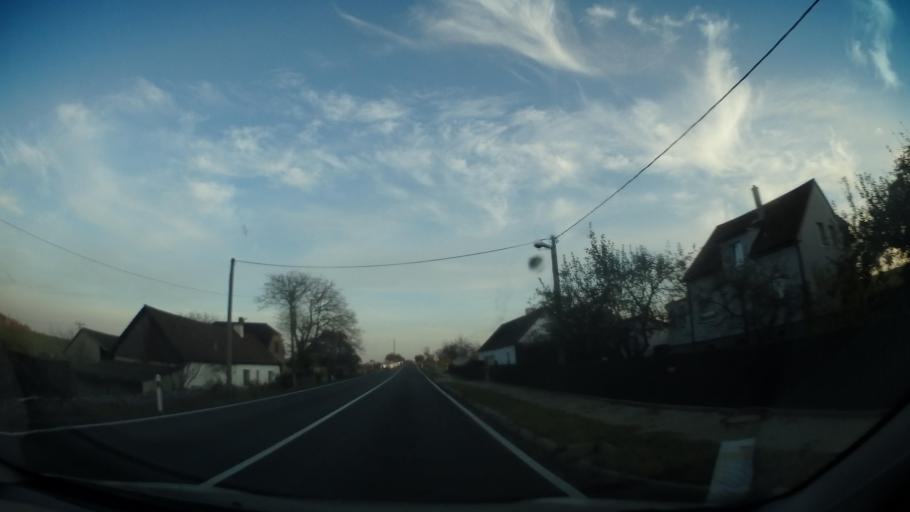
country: CZ
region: Central Bohemia
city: Vlasim
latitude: 49.6865
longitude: 14.9383
